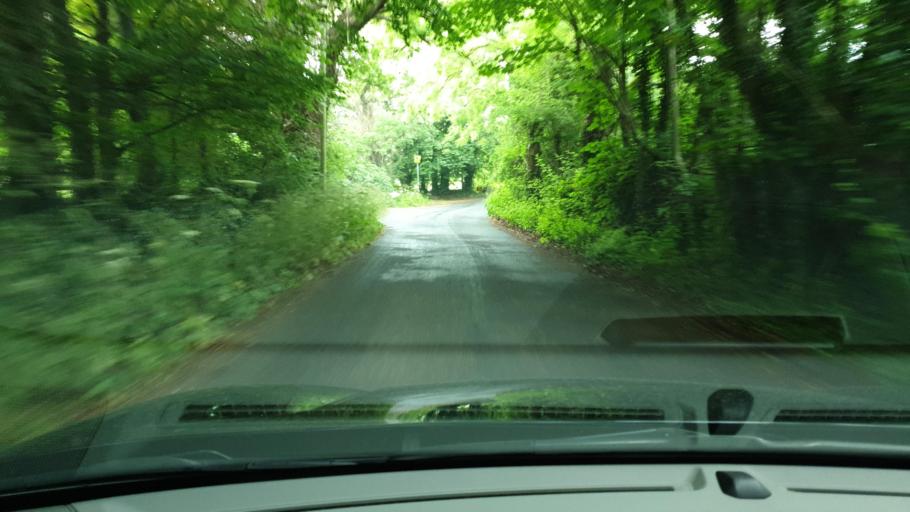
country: IE
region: Leinster
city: Hartstown
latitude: 53.4217
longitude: -6.4103
